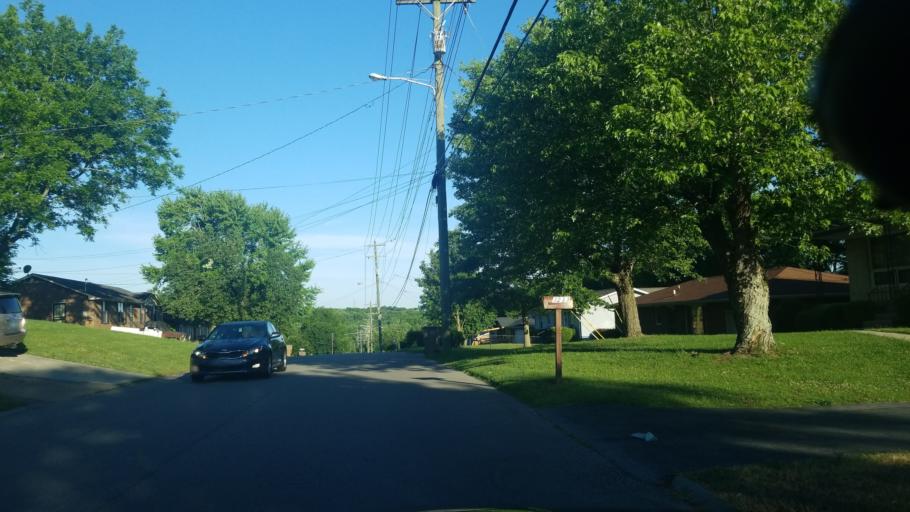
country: US
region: Tennessee
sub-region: Davidson County
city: Nashville
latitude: 36.2425
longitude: -86.7756
